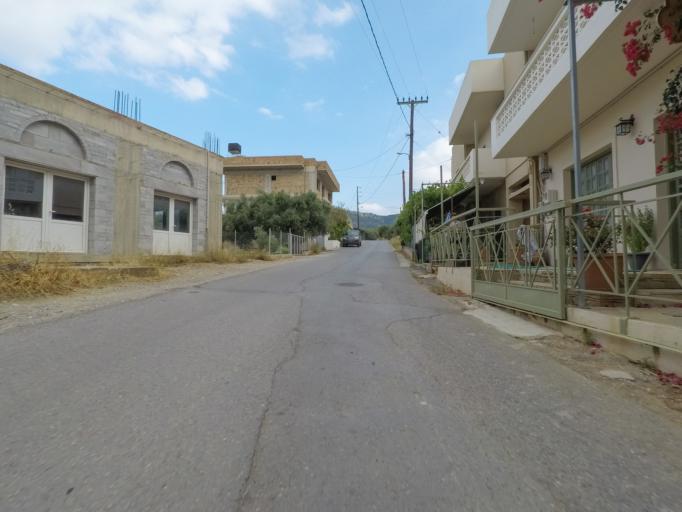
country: GR
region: Crete
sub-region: Nomos Lasithiou
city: Kritsa
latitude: 35.1586
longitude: 25.6484
